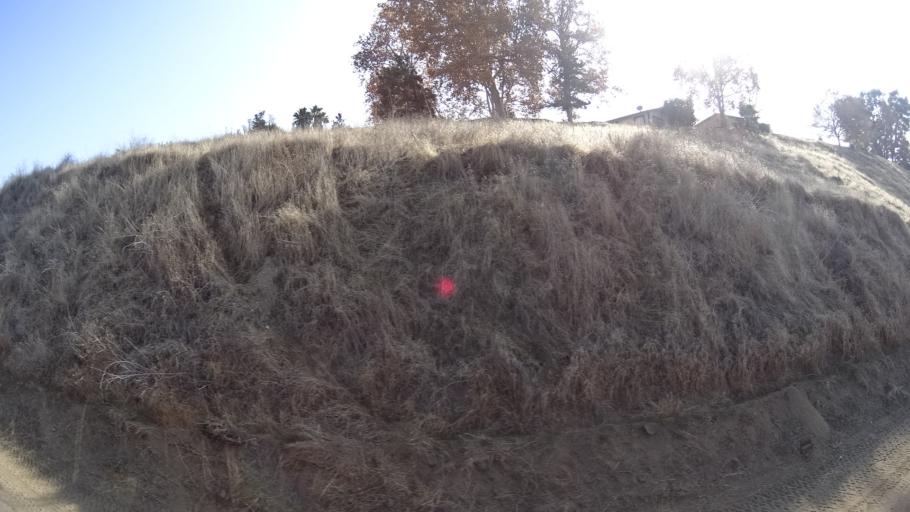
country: US
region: California
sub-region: Kern County
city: Oildale
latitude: 35.4337
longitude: -118.8757
